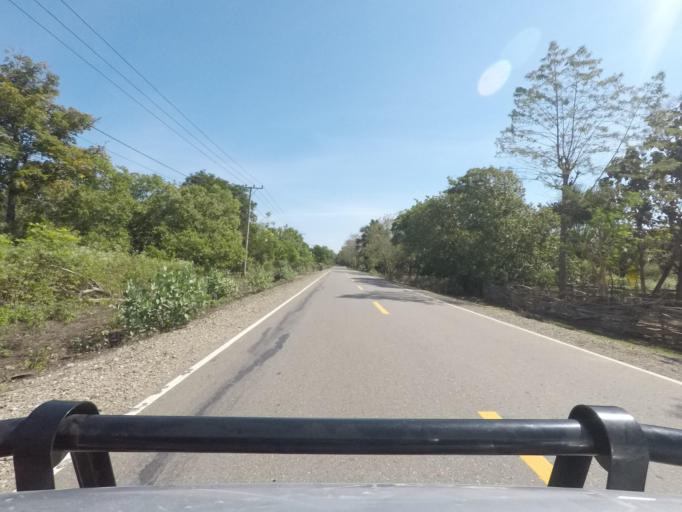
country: TL
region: Bobonaro
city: Maliana
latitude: -8.8939
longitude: 125.0096
